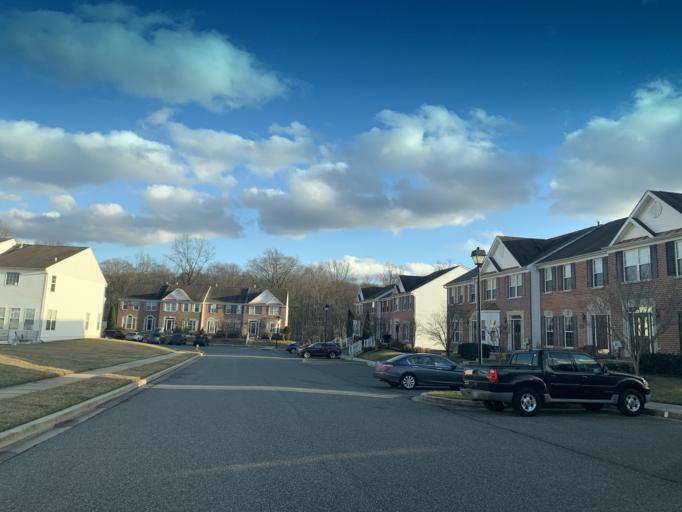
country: US
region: Maryland
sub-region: Harford County
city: South Bel Air
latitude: 39.5347
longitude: -76.3156
